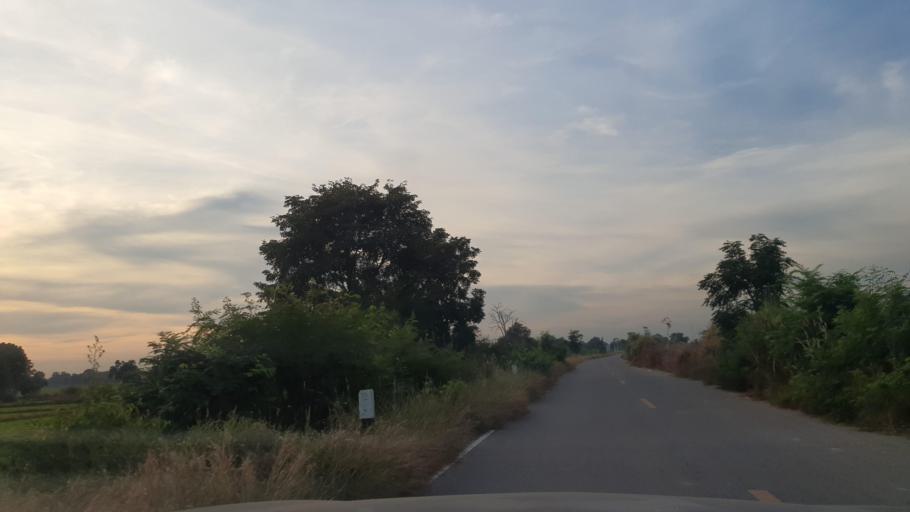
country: TH
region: Uthai Thani
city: Sawang Arom
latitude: 15.7136
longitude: 99.9567
